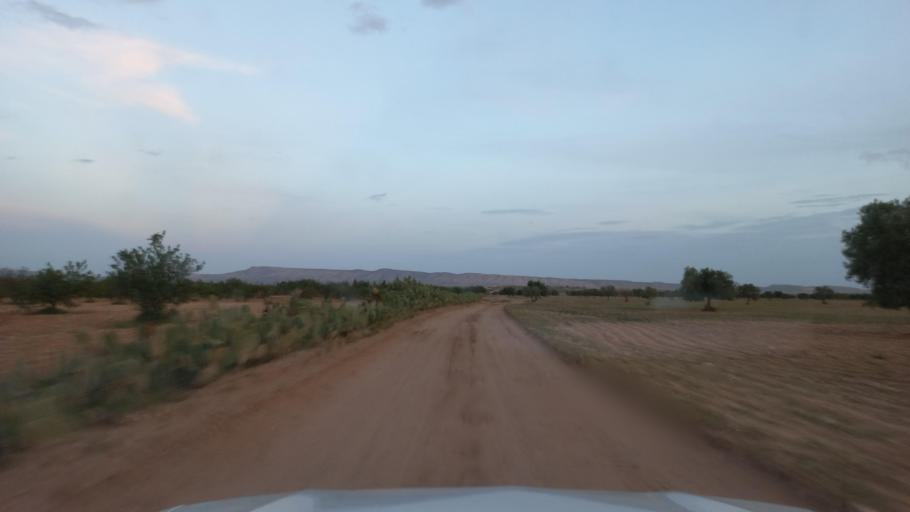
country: TN
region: Al Qasrayn
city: Sbiba
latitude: 35.3485
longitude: 9.0490
